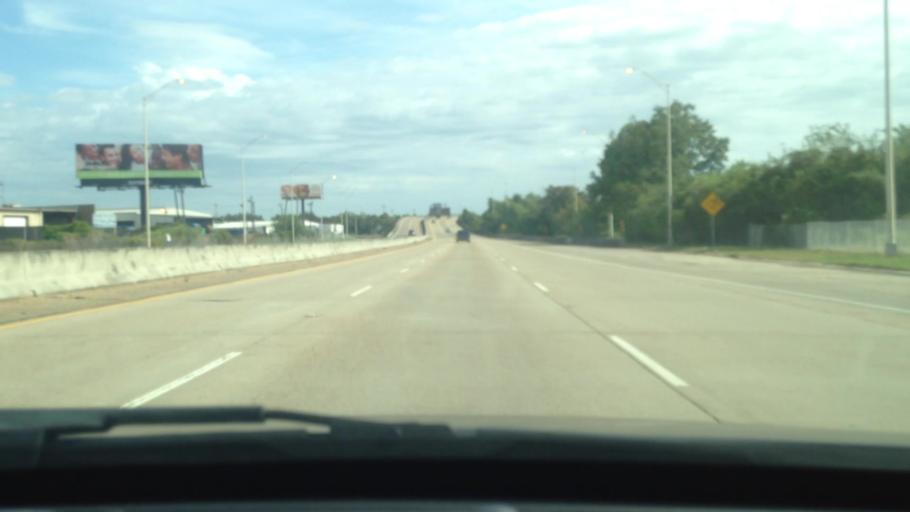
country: US
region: Louisiana
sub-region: Jefferson Parish
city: Jefferson
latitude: 29.9694
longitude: -90.1380
